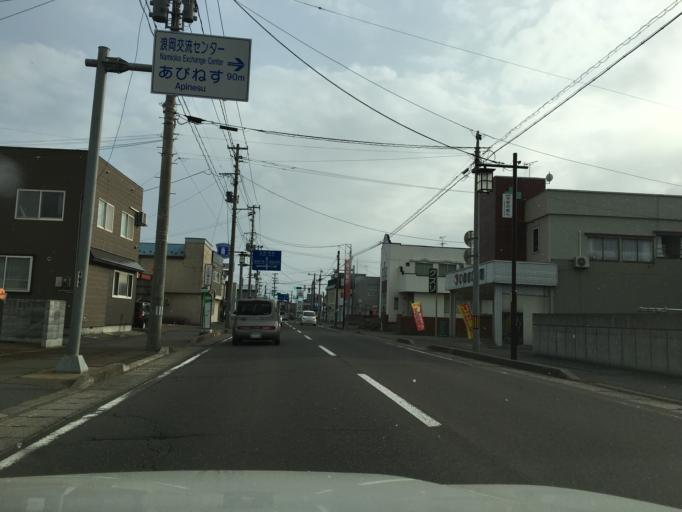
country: JP
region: Aomori
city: Namioka
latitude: 40.7125
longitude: 140.5903
